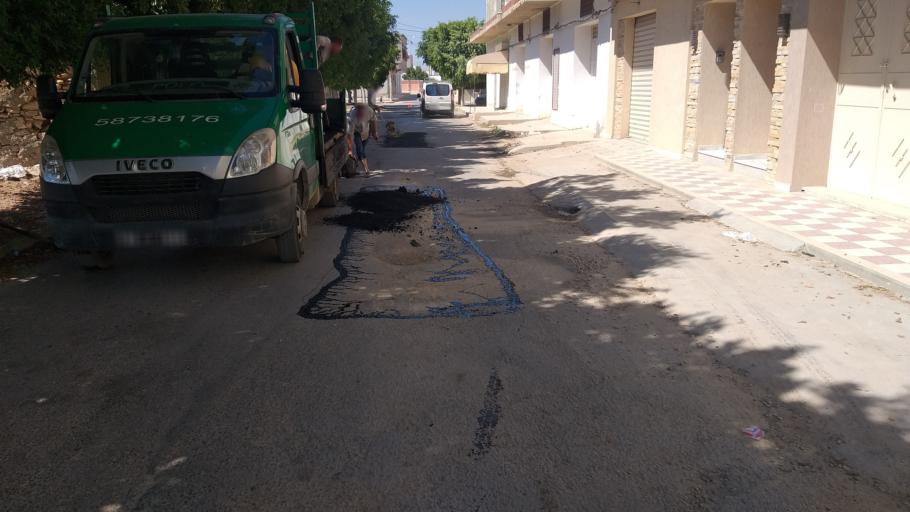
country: TN
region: Al Mahdiyah
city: El Jem
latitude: 35.2966
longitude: 10.7022
